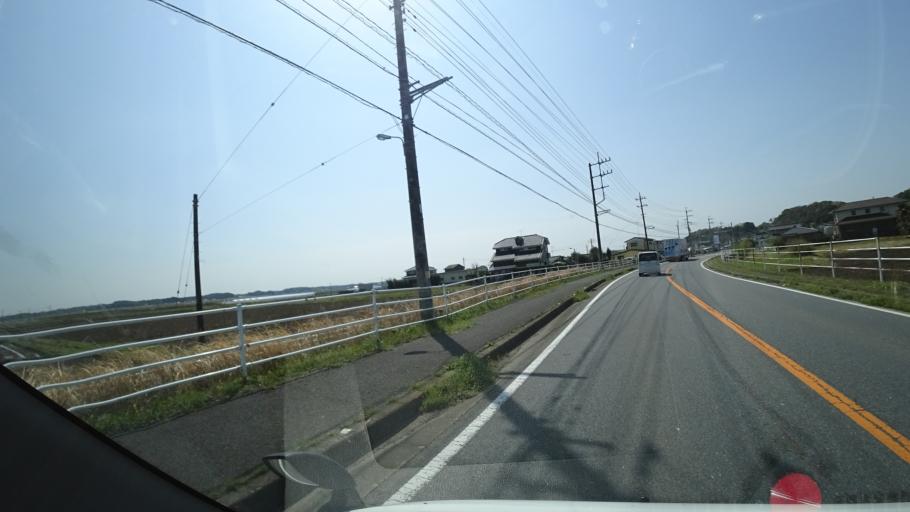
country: JP
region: Chiba
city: Narita
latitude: 35.8538
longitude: 140.2987
